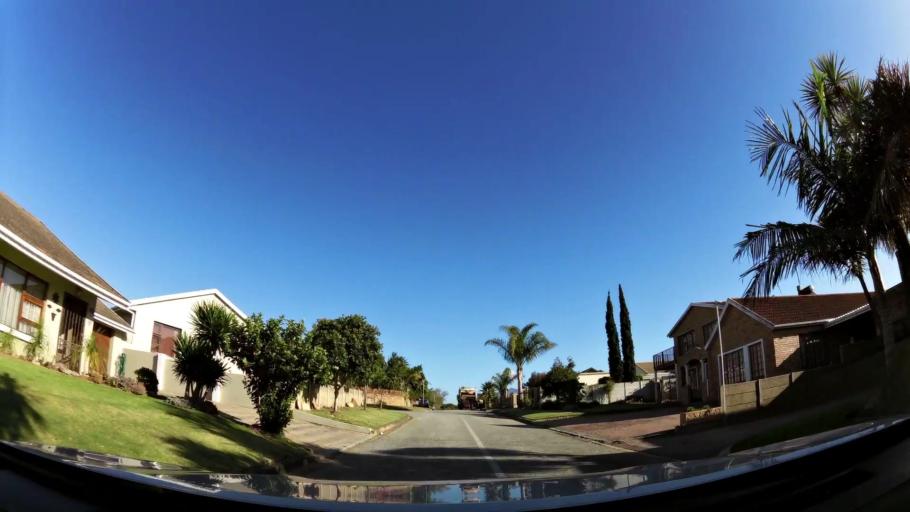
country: ZA
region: Western Cape
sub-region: Eden District Municipality
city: George
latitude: -33.9696
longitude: 22.4410
